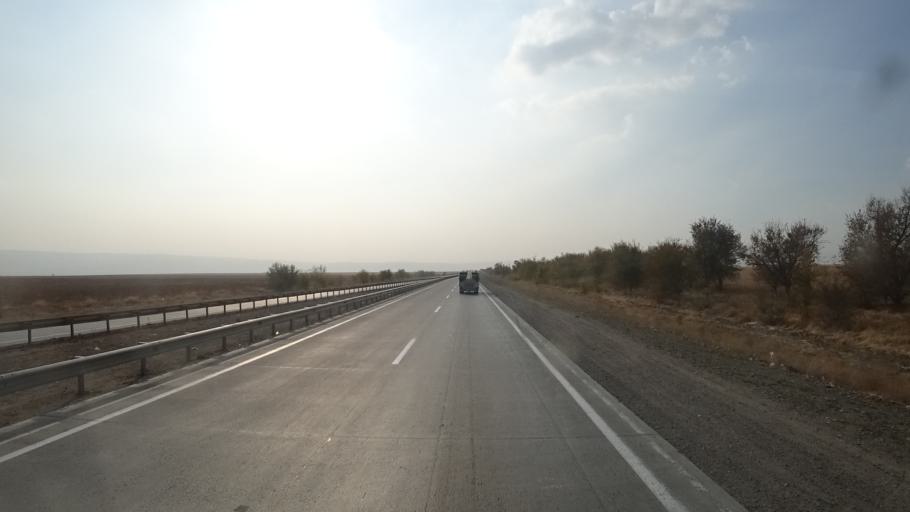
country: KZ
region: Zhambyl
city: Taraz
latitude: 42.8111
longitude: 71.1286
